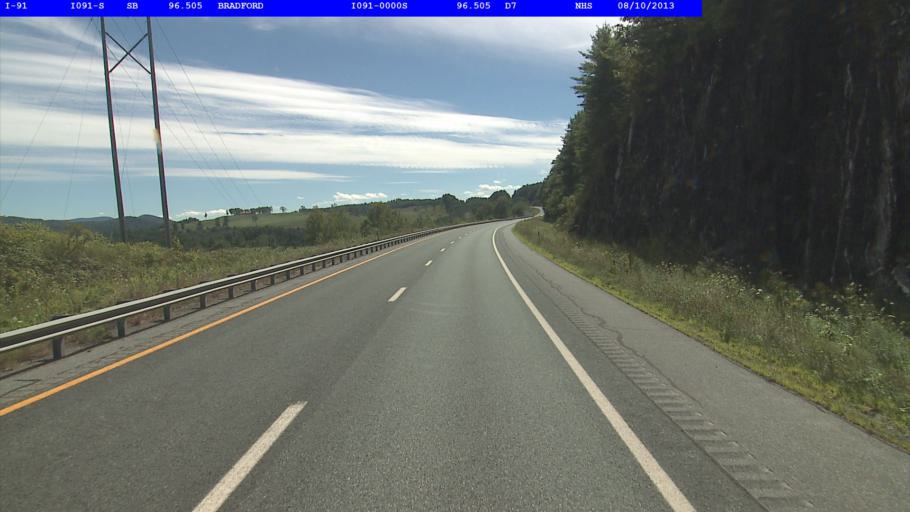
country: US
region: New Hampshire
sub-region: Grafton County
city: Orford
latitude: 43.9689
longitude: -72.1264
